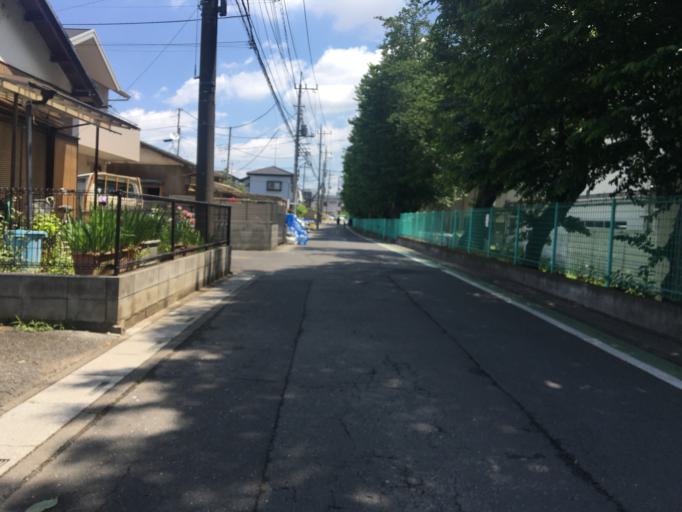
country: JP
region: Saitama
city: Yono
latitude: 35.8880
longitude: 139.6076
